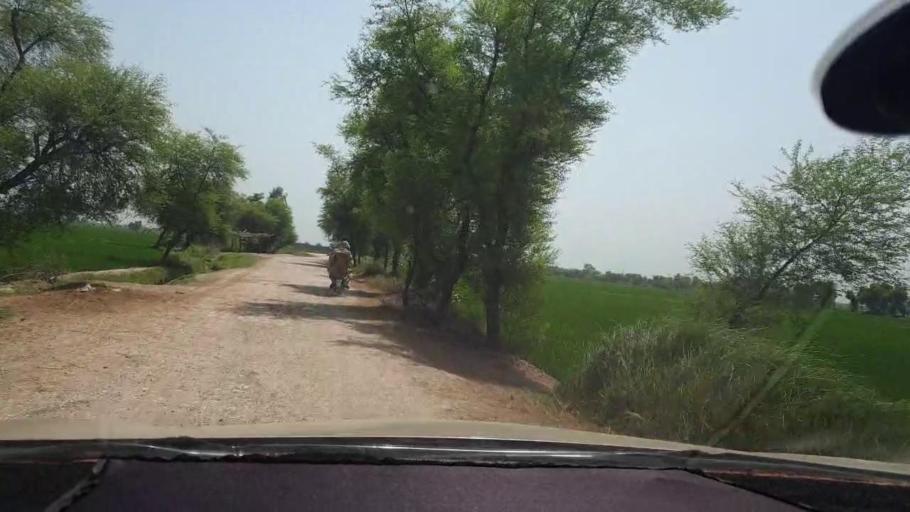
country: PK
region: Sindh
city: Kambar
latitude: 27.6822
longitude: 67.9386
